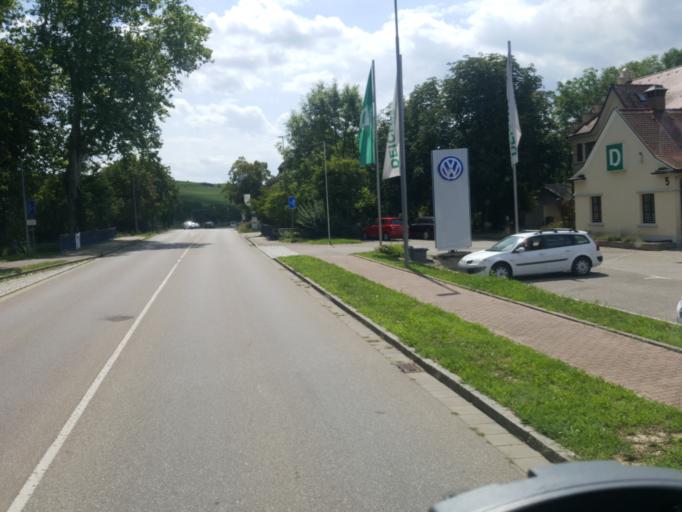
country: DE
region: Baden-Wuerttemberg
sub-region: Freiburg Region
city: Mullheim
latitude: 47.8106
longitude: 7.6093
